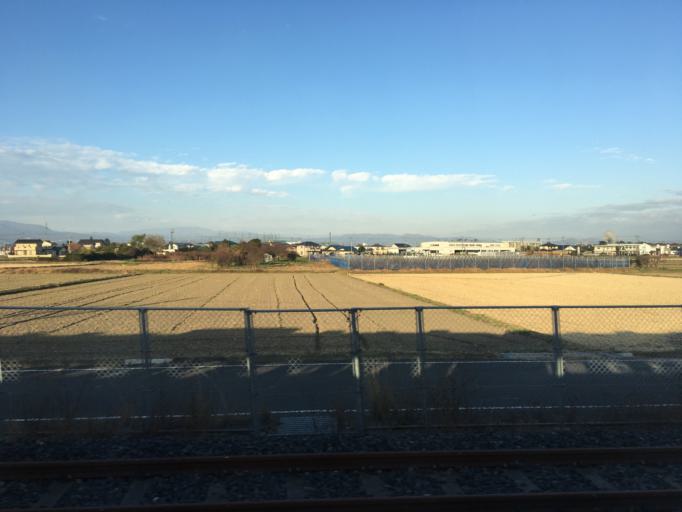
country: JP
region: Gunma
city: Isesaki
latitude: 36.3338
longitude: 139.1786
